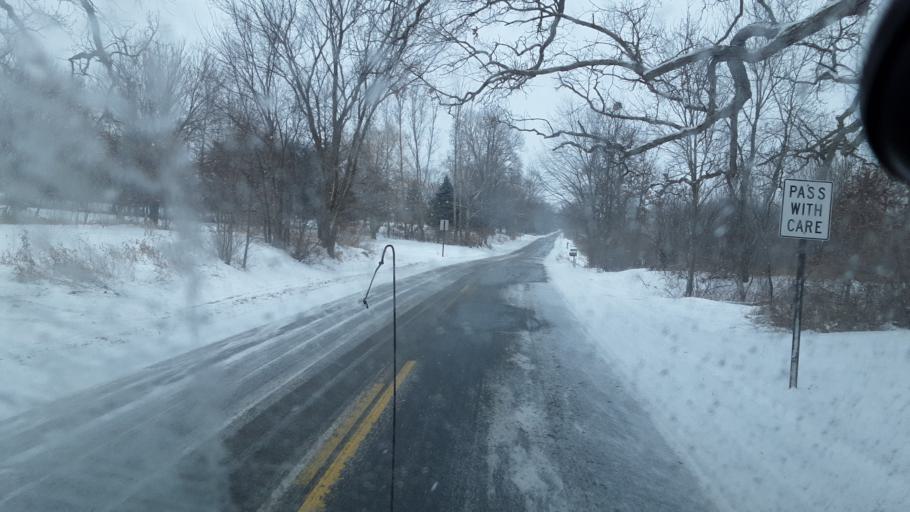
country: US
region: Michigan
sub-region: Ingham County
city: Leslie
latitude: 42.4576
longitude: -84.3136
